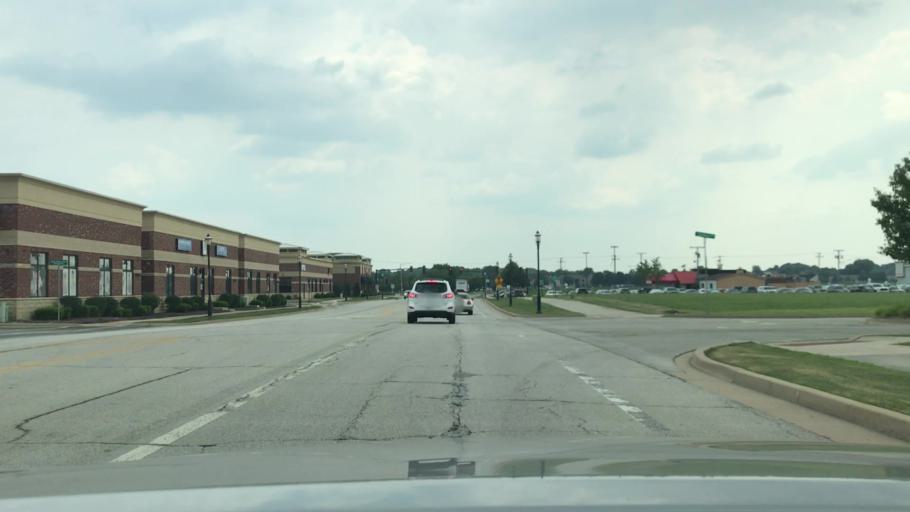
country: US
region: Illinois
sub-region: Will County
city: Plainfield
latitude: 41.6102
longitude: -88.2158
